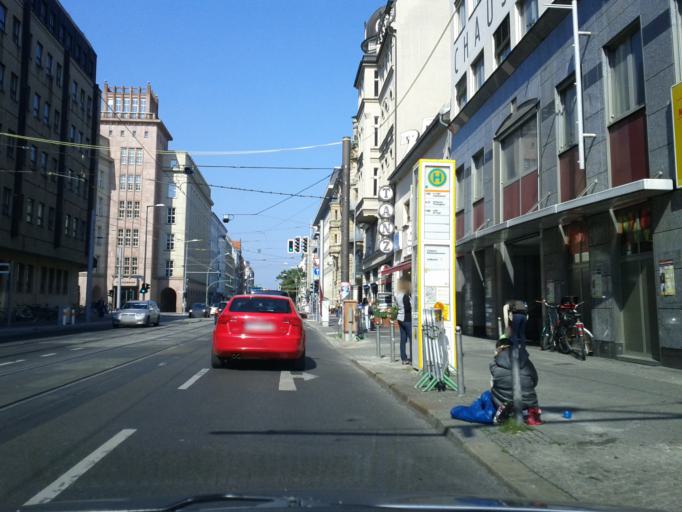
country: DE
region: Berlin
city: Gesundbrunnen
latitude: 52.5301
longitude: 13.3838
